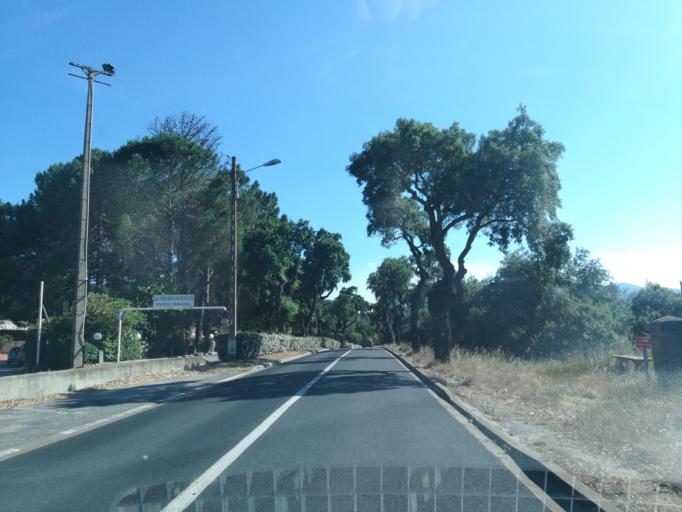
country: FR
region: Languedoc-Roussillon
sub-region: Departement des Pyrenees-Orientales
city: el Volo
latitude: 42.5129
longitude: 2.8296
